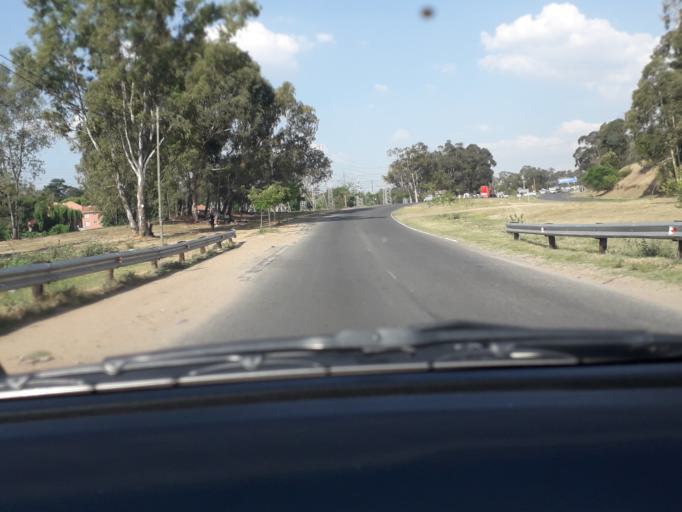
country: ZA
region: Gauteng
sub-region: City of Johannesburg Metropolitan Municipality
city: Modderfontein
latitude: -26.1277
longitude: 28.1213
